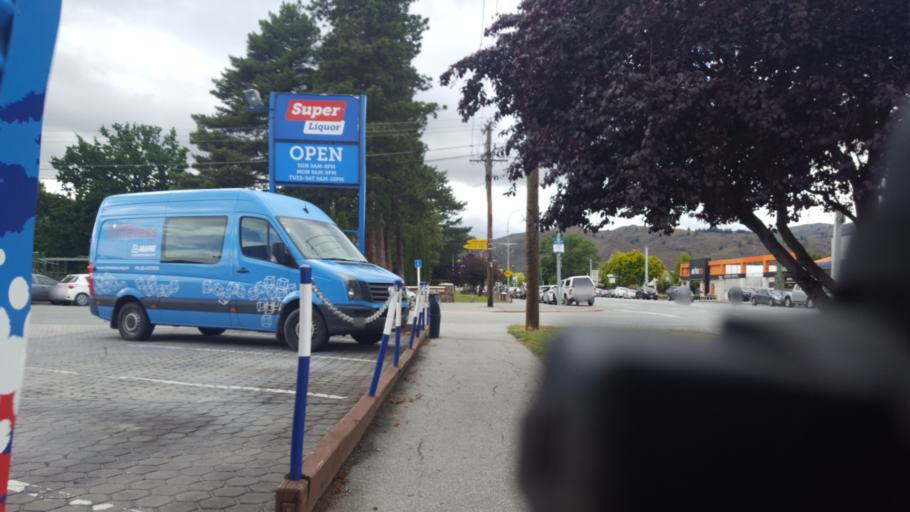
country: NZ
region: Otago
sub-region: Queenstown-Lakes District
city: Wanaka
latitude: -45.2532
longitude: 169.3903
